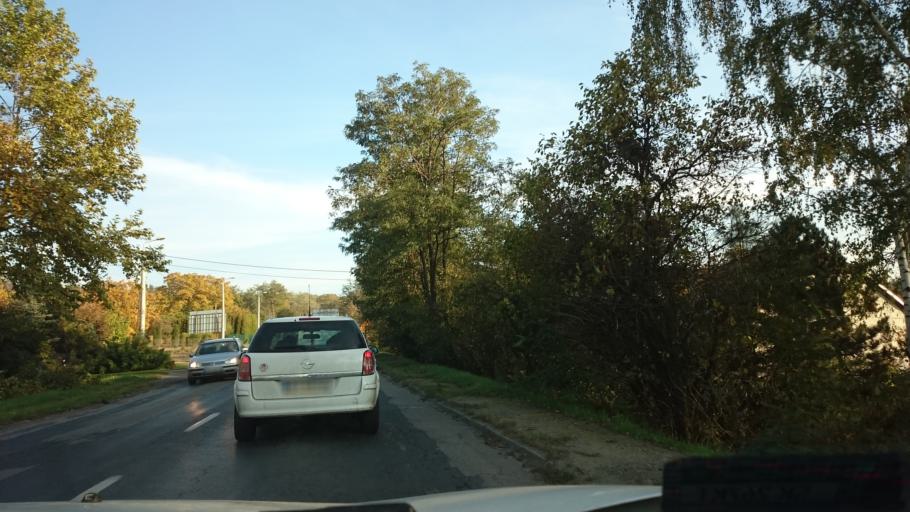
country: PL
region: Silesian Voivodeship
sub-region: Powiat raciborski
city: Pogrzebien
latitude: 50.0835
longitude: 18.2738
